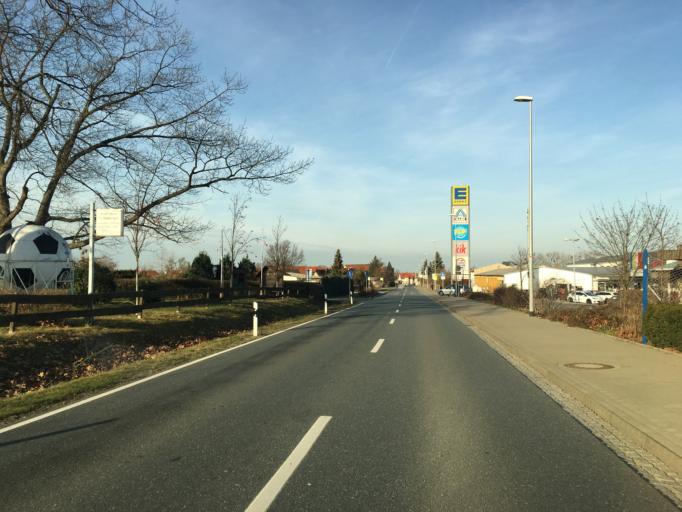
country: DE
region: Saxony
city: Oschatz
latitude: 51.2901
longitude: 13.1233
